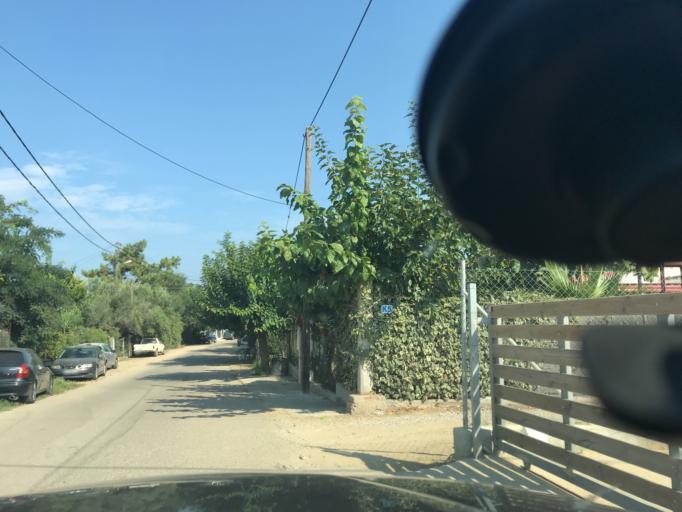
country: GR
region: West Greece
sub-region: Nomos Ileias
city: Kardamas
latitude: 37.7201
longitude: 21.3118
